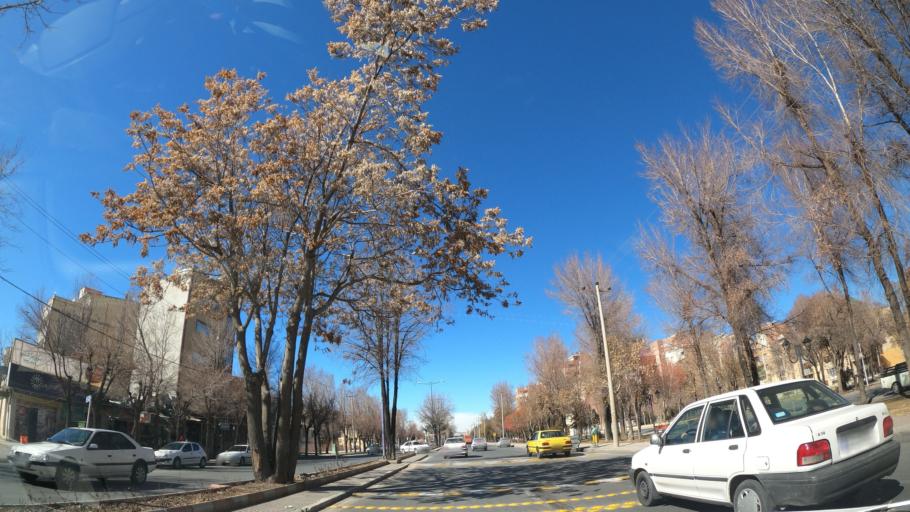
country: IR
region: Chahar Mahall va Bakhtiari
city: Shahrekord
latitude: 32.3131
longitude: 50.8788
